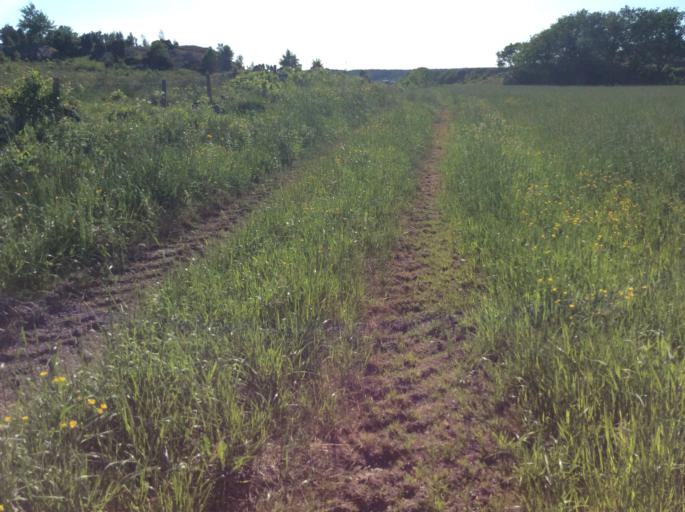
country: SE
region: Vaestra Goetaland
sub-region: Goteborg
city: Majorna
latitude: 57.7989
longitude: 11.8721
